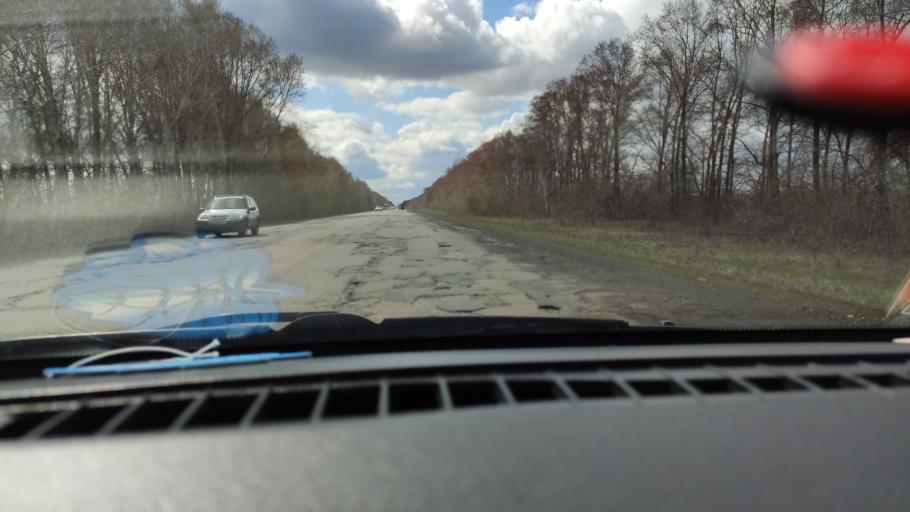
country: RU
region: Samara
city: Tol'yatti
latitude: 53.6431
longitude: 49.4208
